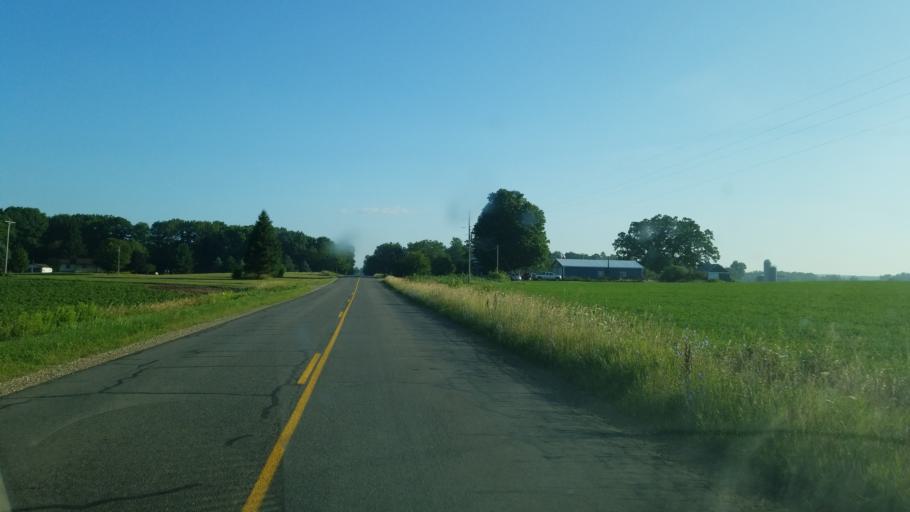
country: US
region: Michigan
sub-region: Montcalm County
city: Lakeview
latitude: 43.5328
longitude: -85.1847
